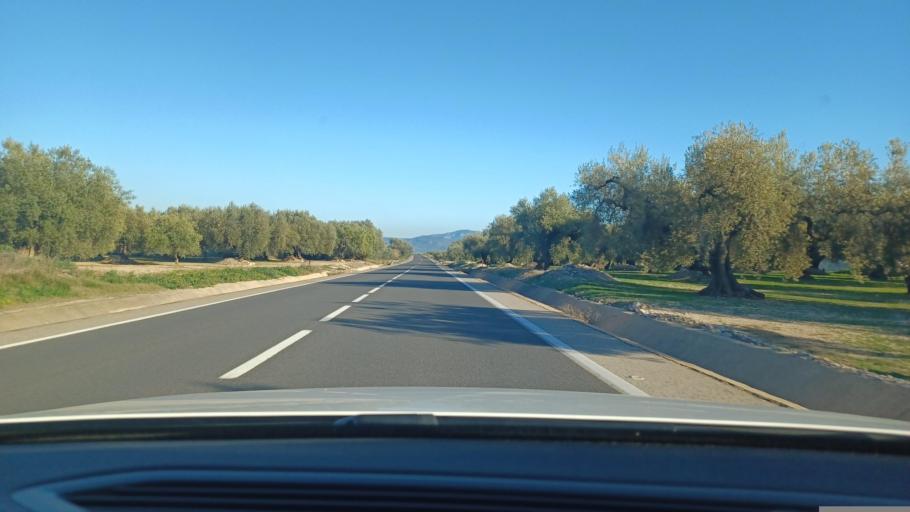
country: ES
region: Catalonia
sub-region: Provincia de Tarragona
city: Mas de Barberans
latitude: 40.6414
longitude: 0.3614
